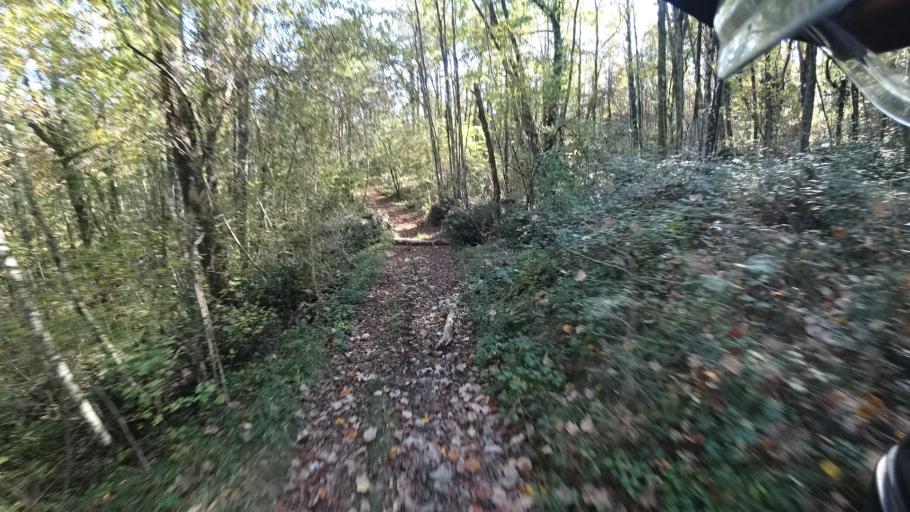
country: HR
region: Primorsko-Goranska
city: Matulji
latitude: 45.3921
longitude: 14.2941
